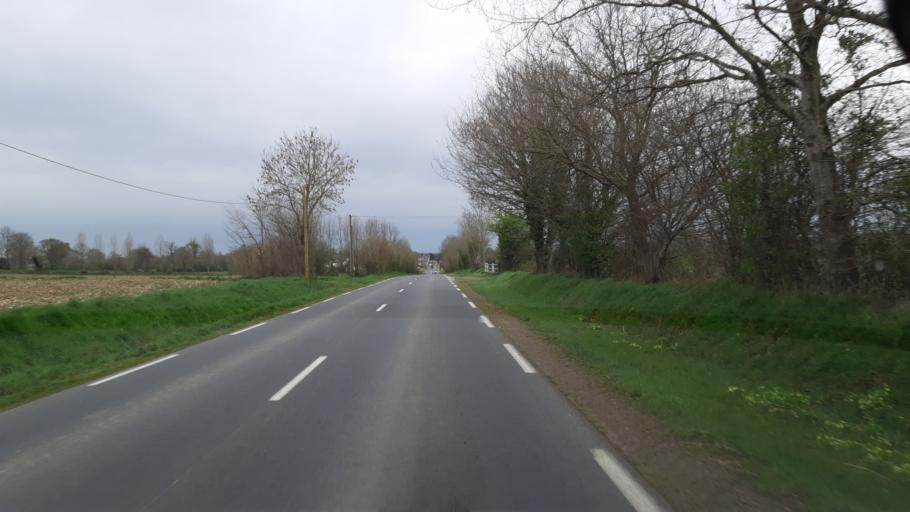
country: FR
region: Lower Normandy
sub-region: Departement de la Manche
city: Hambye
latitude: 48.9500
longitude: -1.2507
